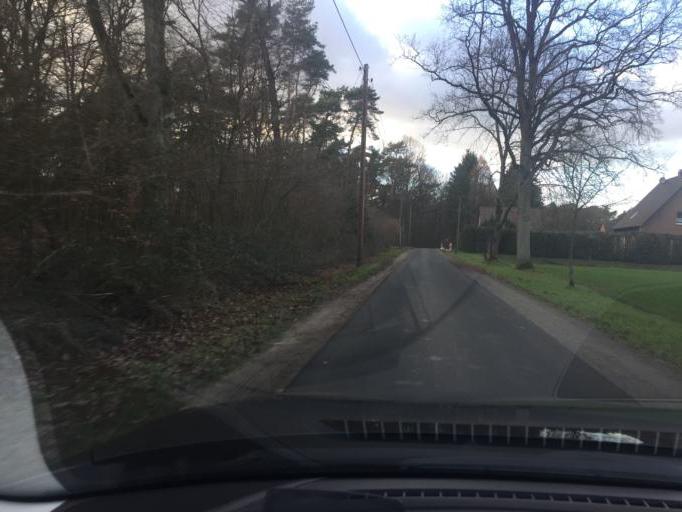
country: DE
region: North Rhine-Westphalia
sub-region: Regierungsbezirk Dusseldorf
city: Schermbeck
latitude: 51.6978
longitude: 6.8581
